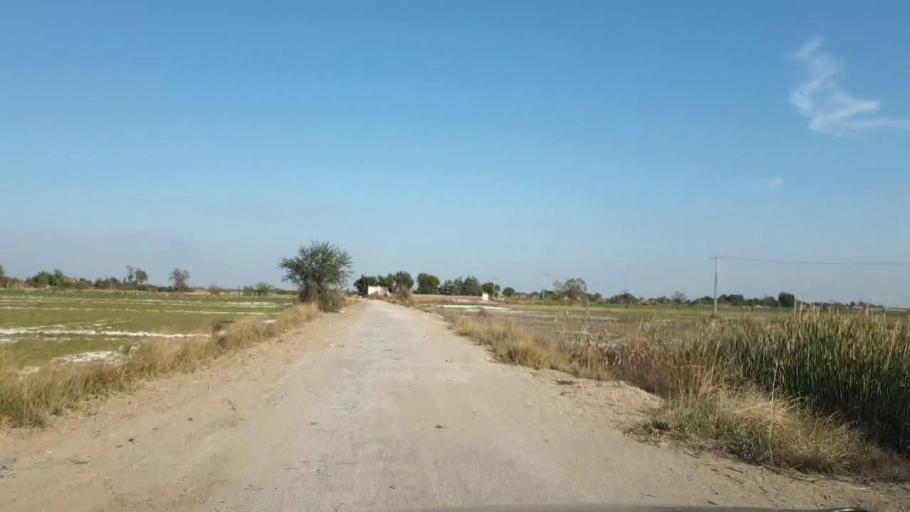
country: PK
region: Sindh
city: Khadro
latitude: 26.1901
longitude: 68.7637
